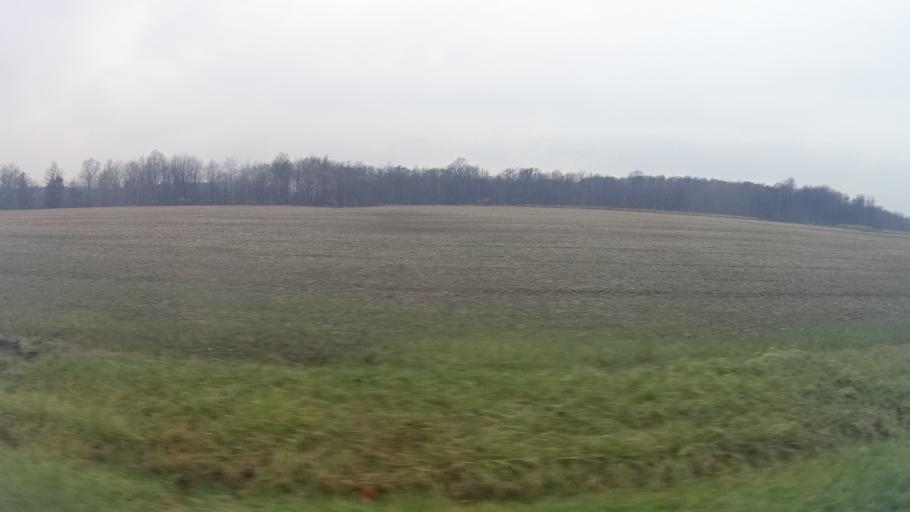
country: US
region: Ohio
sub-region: Lorain County
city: Lagrange
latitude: 41.2702
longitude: -82.1574
